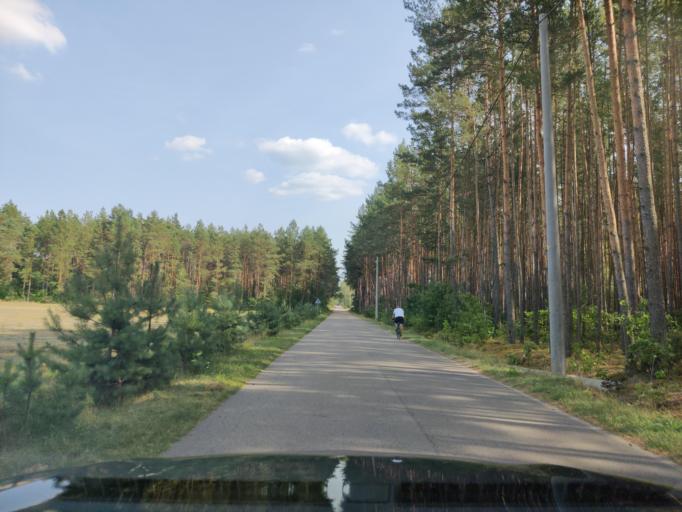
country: PL
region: Masovian Voivodeship
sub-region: Powiat makowski
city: Rozan
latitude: 52.8469
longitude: 21.4636
